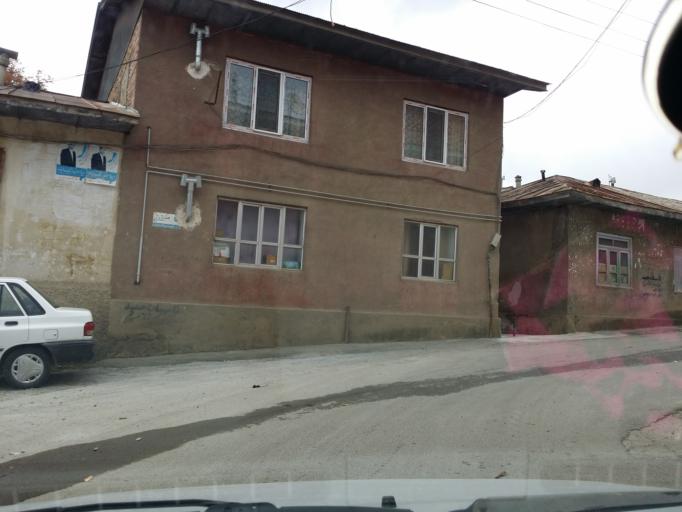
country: IR
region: Mazandaran
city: `Abbasabad
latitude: 36.5031
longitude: 51.1500
